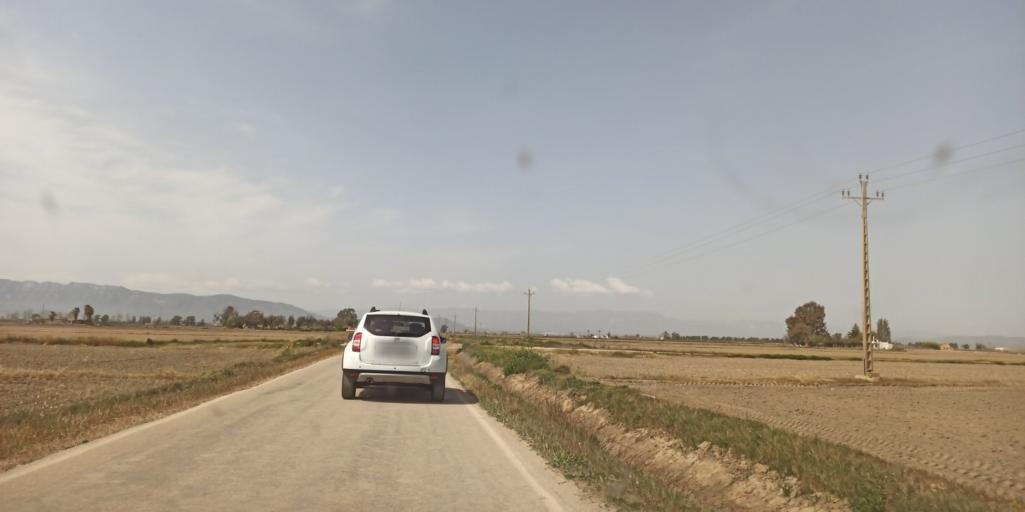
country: ES
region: Catalonia
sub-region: Provincia de Tarragona
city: Deltebre
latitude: 40.6448
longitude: 0.7239
